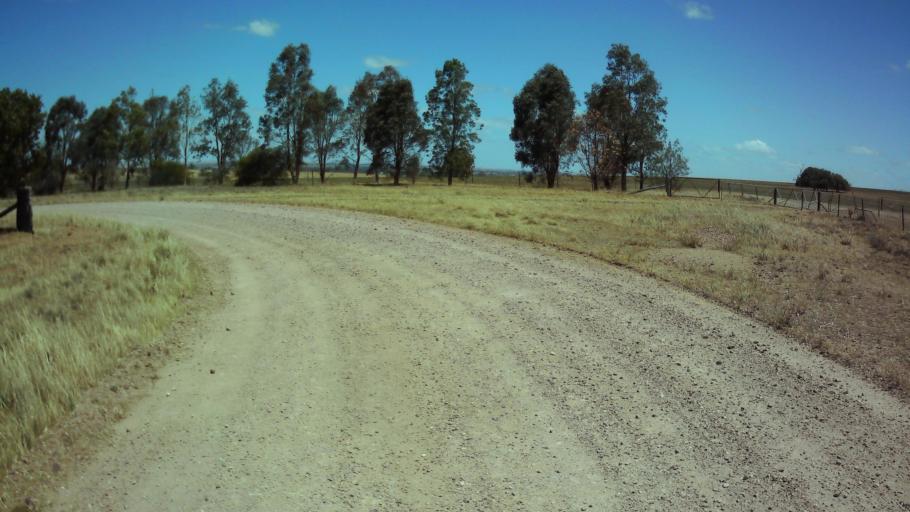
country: AU
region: New South Wales
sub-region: Weddin
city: Grenfell
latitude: -33.9558
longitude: 148.3276
